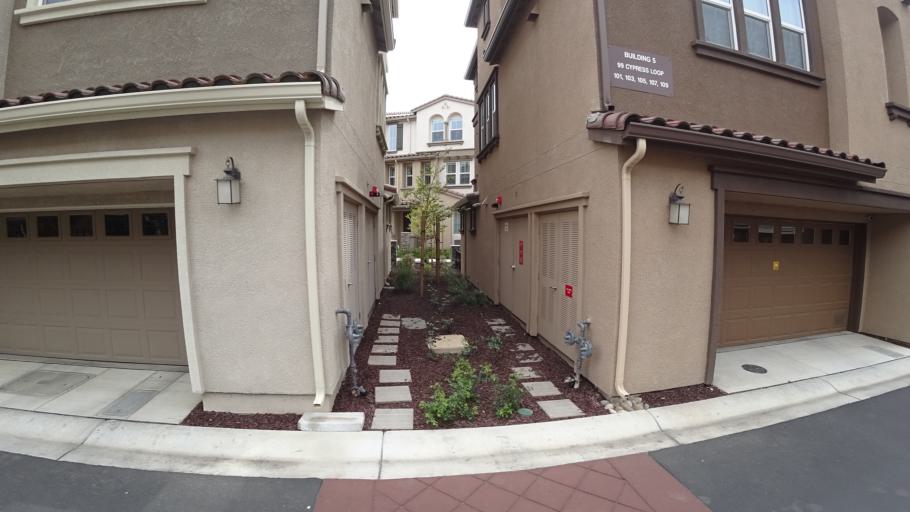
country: US
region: California
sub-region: Alameda County
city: Hayward
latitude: 37.6513
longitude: -122.0696
